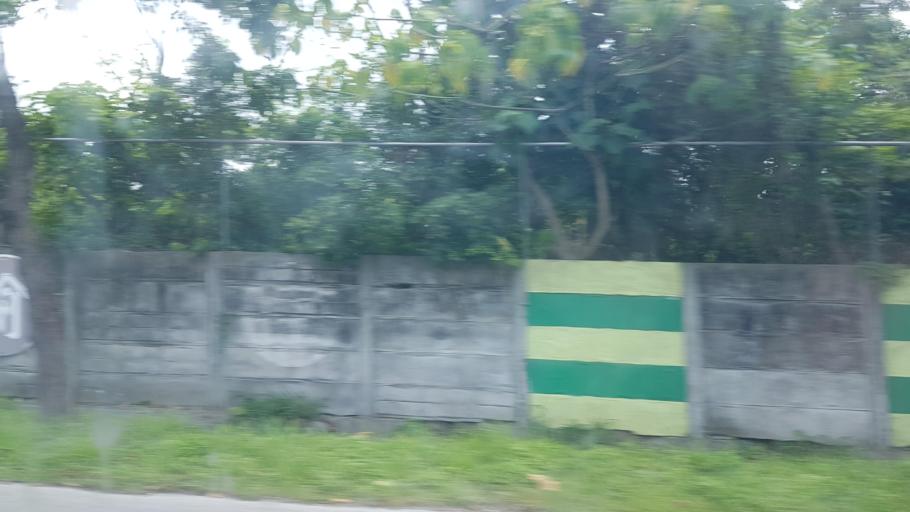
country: TW
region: Taiwan
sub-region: Hualien
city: Hualian
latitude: 23.9258
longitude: 121.5909
